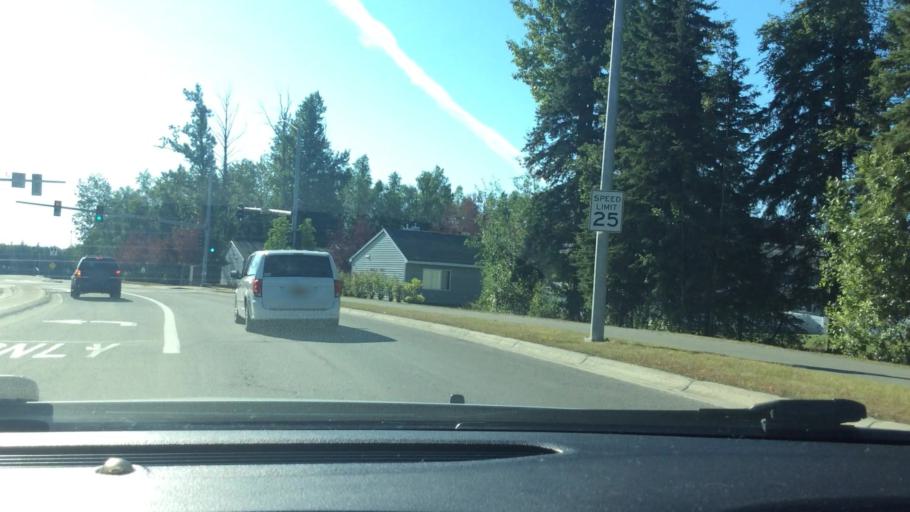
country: US
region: Alaska
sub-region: Anchorage Municipality
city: Anchorage
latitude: 61.2332
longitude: -149.7710
